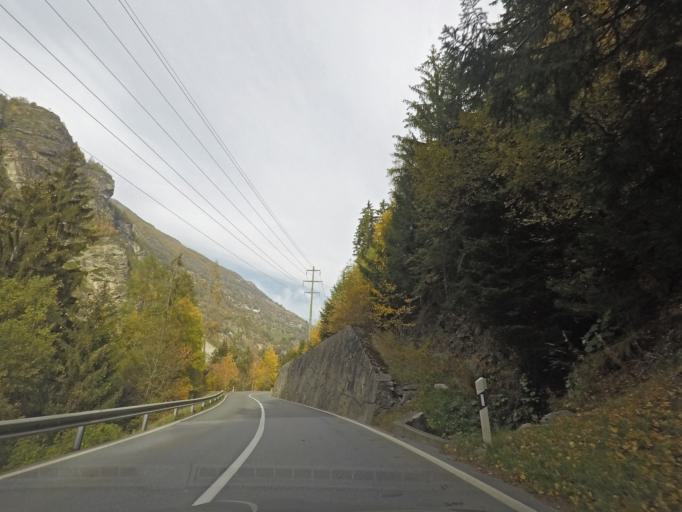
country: CH
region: Valais
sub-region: Visp District
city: Grachen
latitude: 46.1979
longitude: 7.8192
